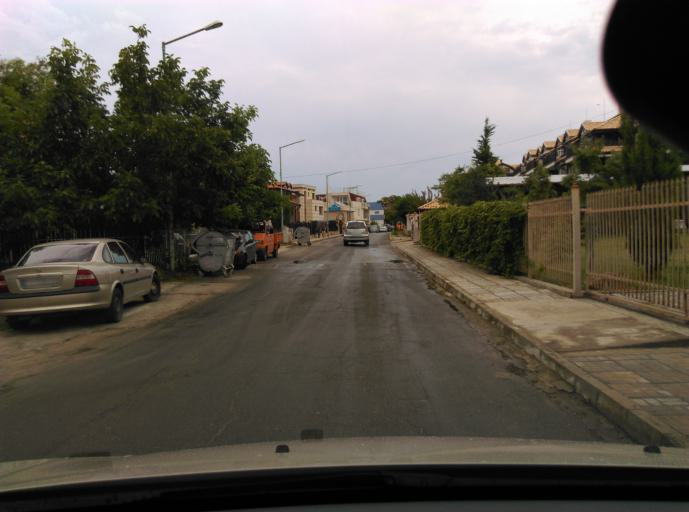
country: BG
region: Burgas
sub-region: Obshtina Sozopol
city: Sozopol
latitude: 42.4075
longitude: 27.7076
